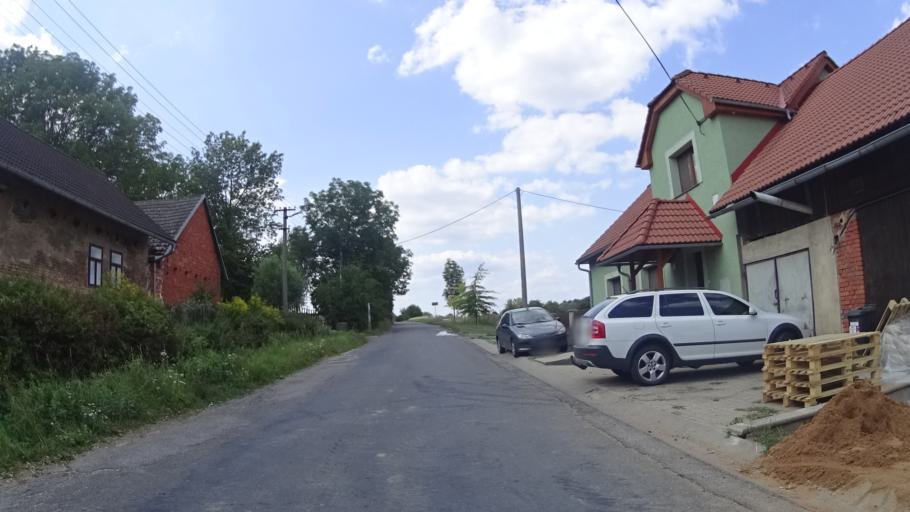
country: CZ
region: Kralovehradecky
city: Kopidlno
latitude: 50.3986
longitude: 15.2826
